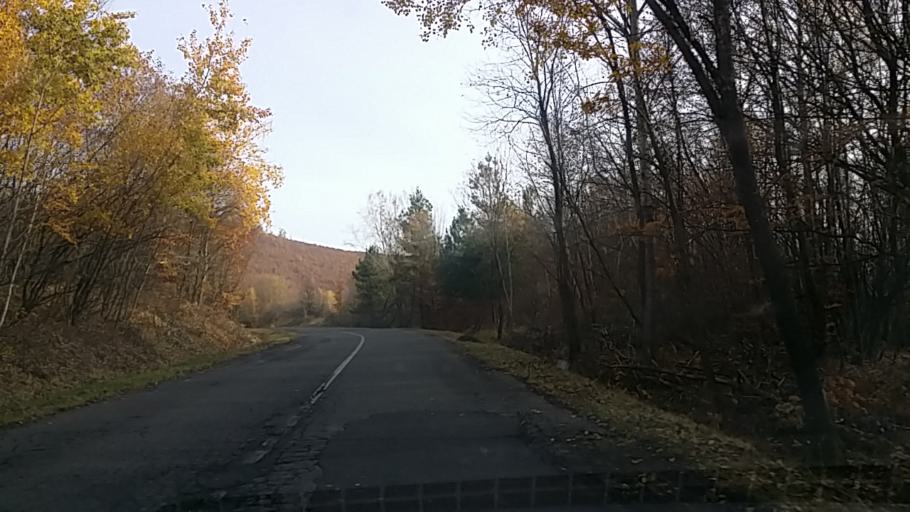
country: HU
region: Borsod-Abauj-Zemplen
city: Gonc
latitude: 48.5538
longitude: 21.3956
